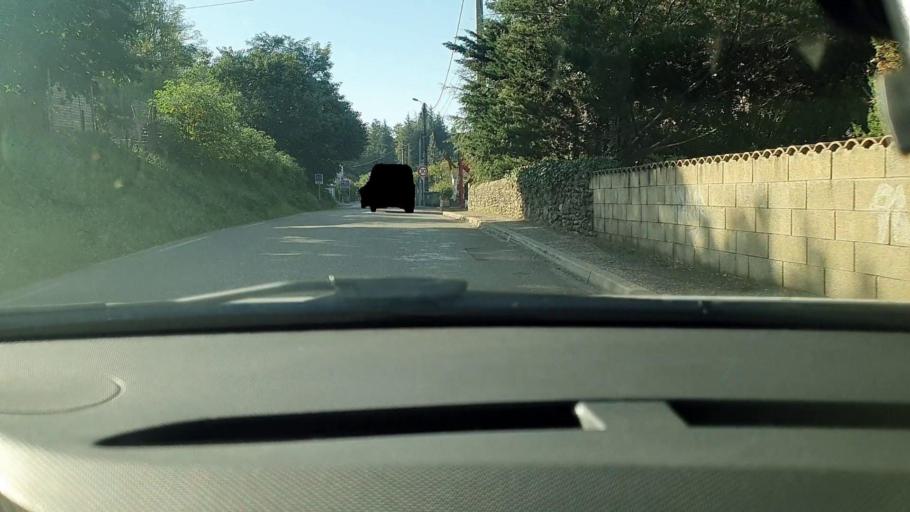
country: FR
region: Languedoc-Roussillon
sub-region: Departement du Gard
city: Besseges
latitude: 44.3026
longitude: 4.1290
